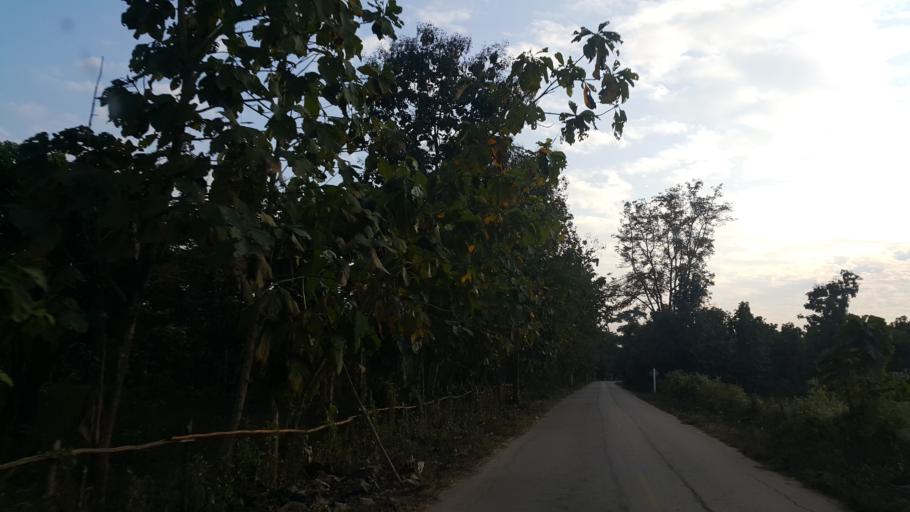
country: TH
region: Lampang
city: Sop Prap
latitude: 17.9254
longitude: 99.3333
